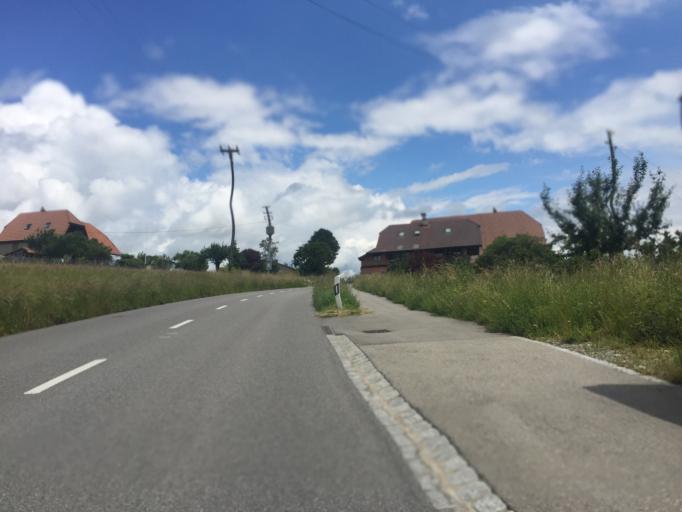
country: CH
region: Bern
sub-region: Bern-Mittelland District
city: Wohlen
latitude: 46.9782
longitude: 7.3658
